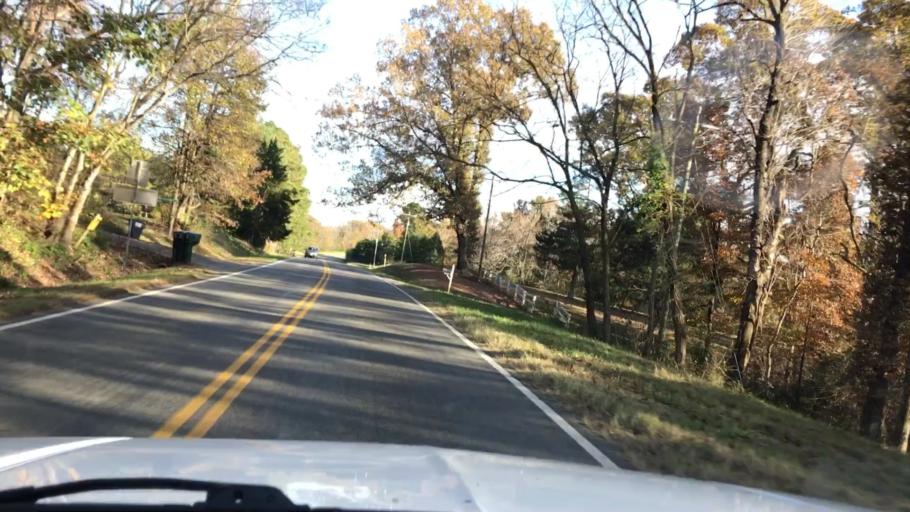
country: US
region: Virginia
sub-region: Goochland County
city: Goochland
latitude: 37.6662
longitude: -77.8776
